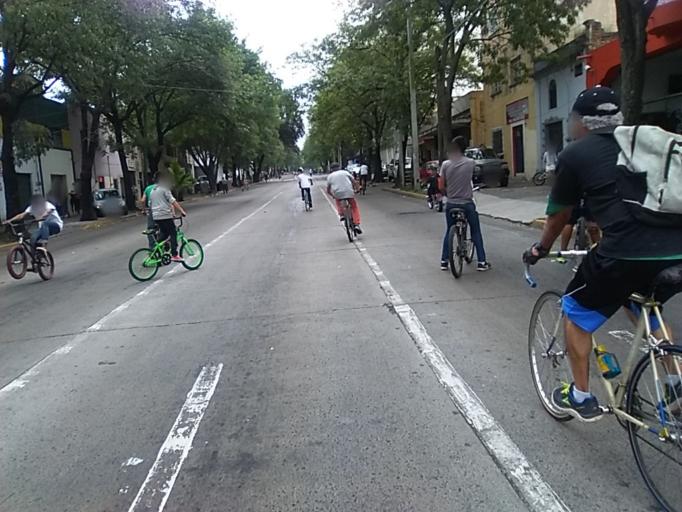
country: MX
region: Jalisco
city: Tlaquepaque
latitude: 20.6721
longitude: -103.3291
